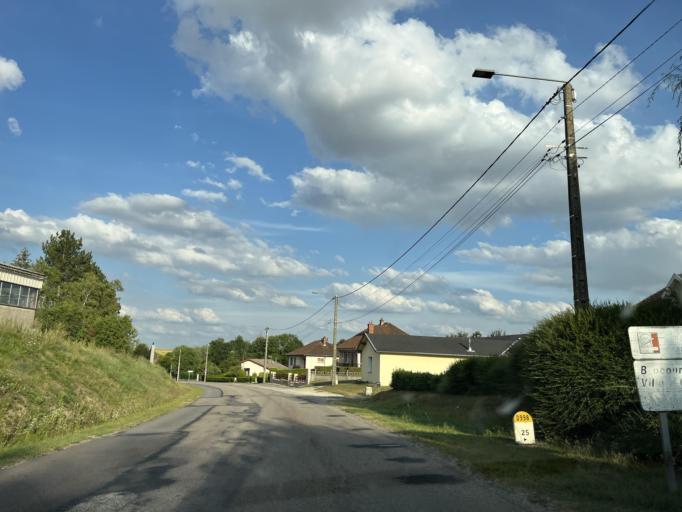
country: FR
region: Lorraine
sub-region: Departement de la Meuse
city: Clermont-en-Argonne
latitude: 49.1007
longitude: 5.0924
